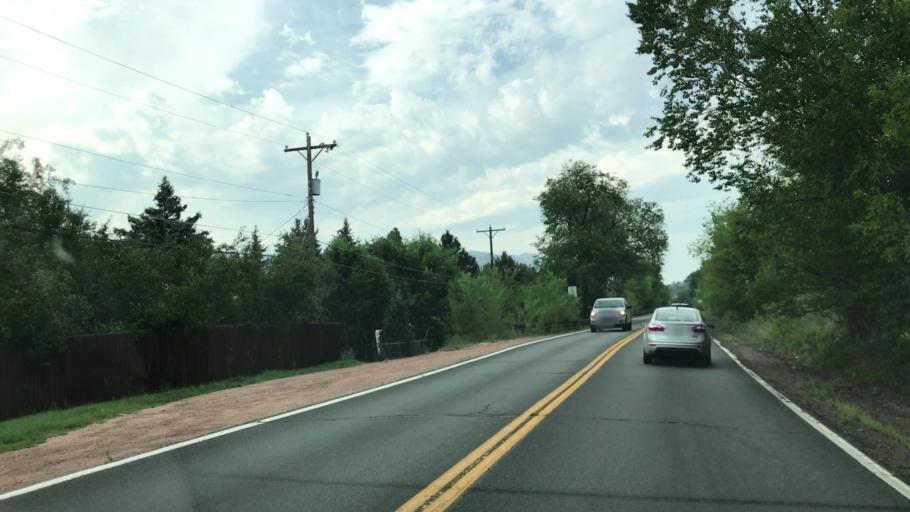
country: US
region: Colorado
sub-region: El Paso County
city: Manitou Springs
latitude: 38.8625
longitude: -104.8660
